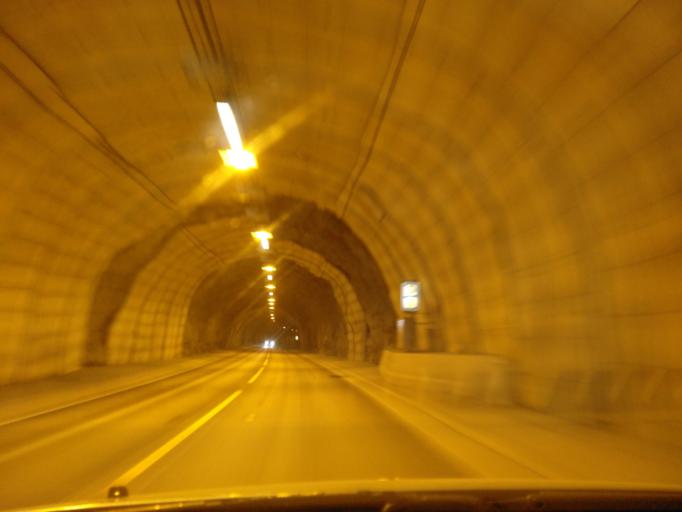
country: NO
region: Rogaland
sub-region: Sauda
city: Sauda
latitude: 59.8449
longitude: 6.3338
